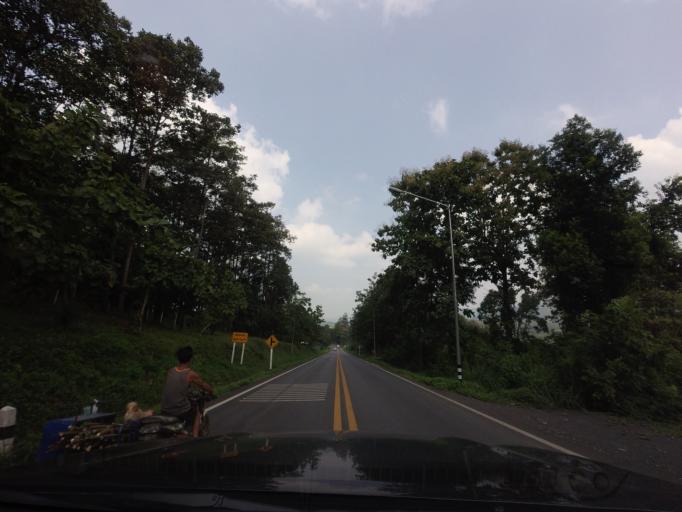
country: TH
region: Nan
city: Pua
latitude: 19.1380
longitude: 100.9483
